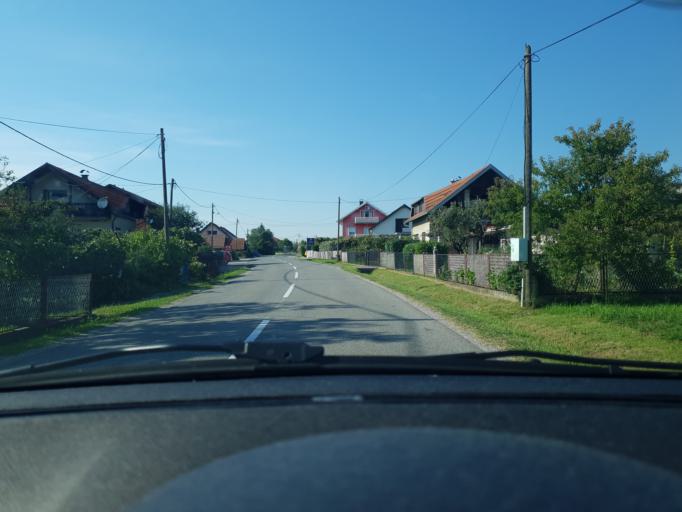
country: HR
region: Zagrebacka
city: Jakovlje
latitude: 45.9344
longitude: 15.8441
